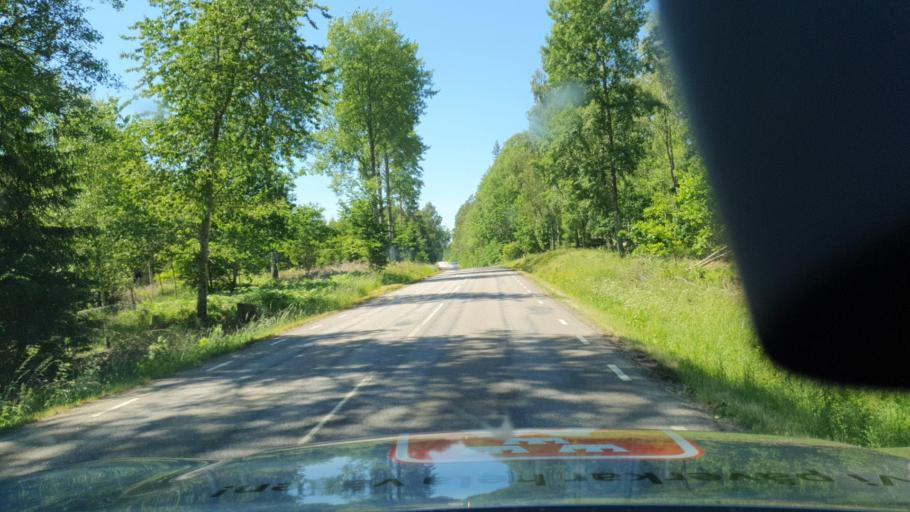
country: SE
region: Kalmar
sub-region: Emmaboda Kommun
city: Emmaboda
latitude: 56.5099
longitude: 15.6574
